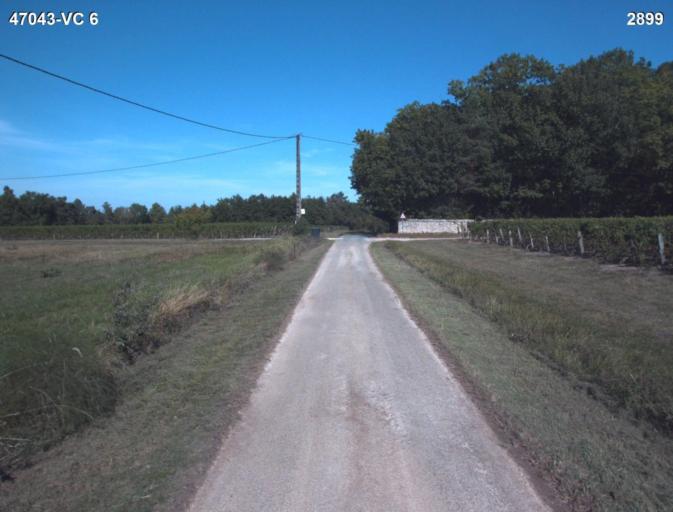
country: FR
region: Aquitaine
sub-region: Departement du Lot-et-Garonne
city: Buzet-sur-Baise
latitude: 44.2301
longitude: 0.2884
